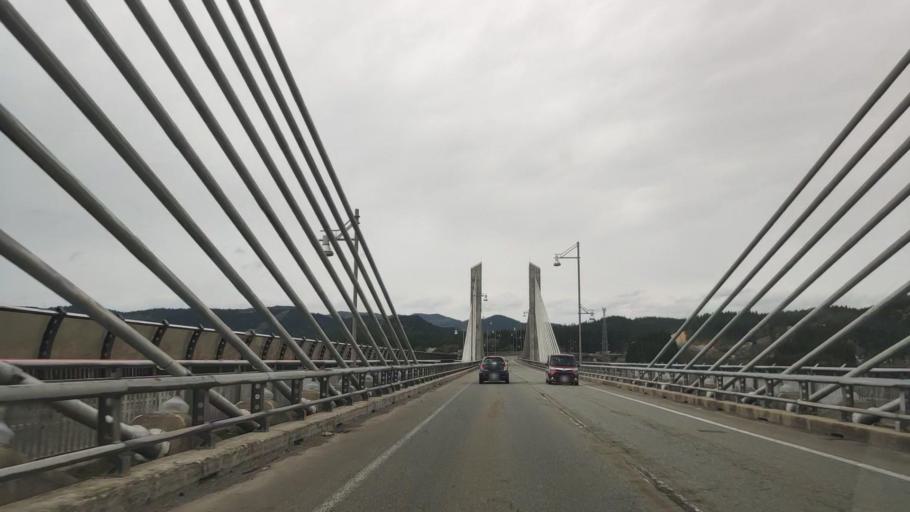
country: JP
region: Akita
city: Takanosu
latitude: 40.2067
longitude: 140.3037
